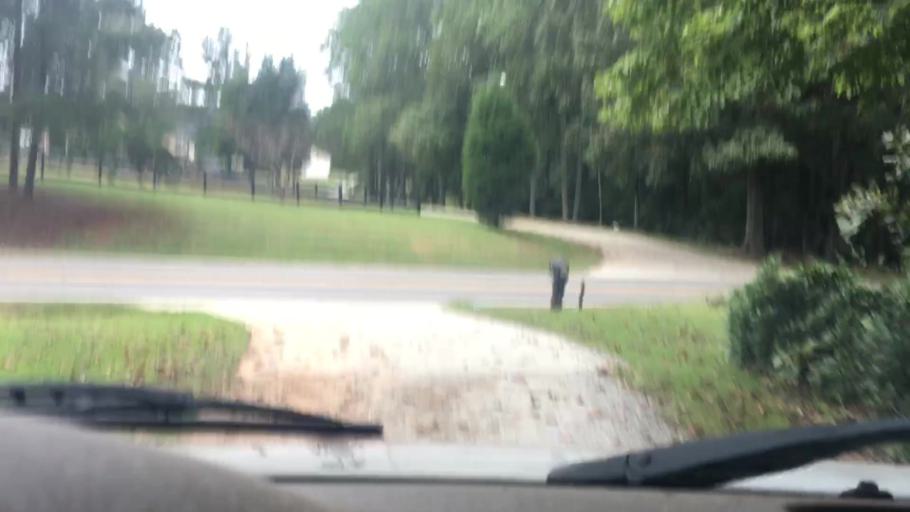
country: US
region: North Carolina
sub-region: Iredell County
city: Mooresville
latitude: 35.6384
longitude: -80.7741
